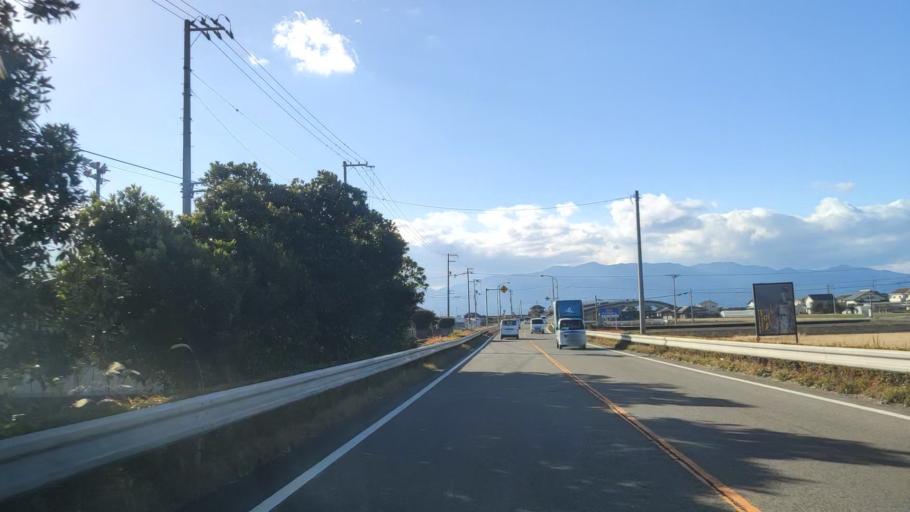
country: JP
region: Ehime
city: Saijo
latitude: 33.9157
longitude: 133.1394
